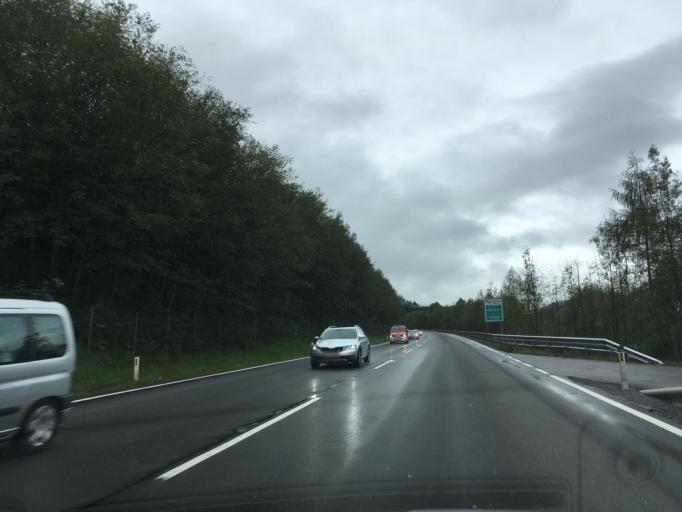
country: AT
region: Salzburg
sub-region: Politischer Bezirk Zell am See
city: Lend
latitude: 47.2964
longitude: 13.0703
